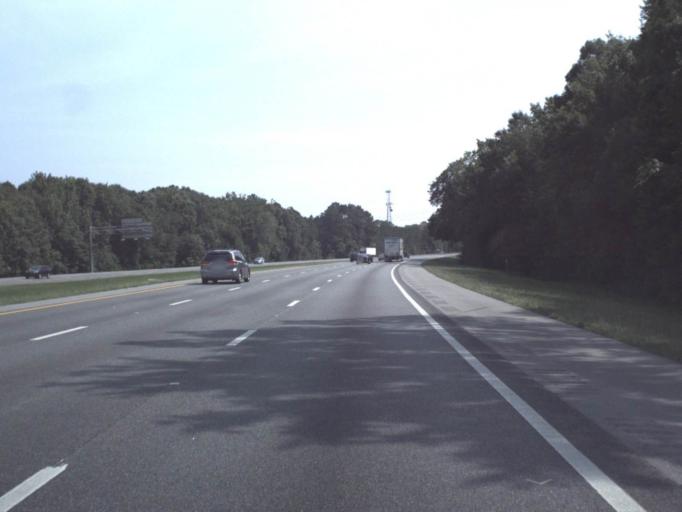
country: US
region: Florida
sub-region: Nassau County
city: Yulee
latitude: 30.7008
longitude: -81.6761
